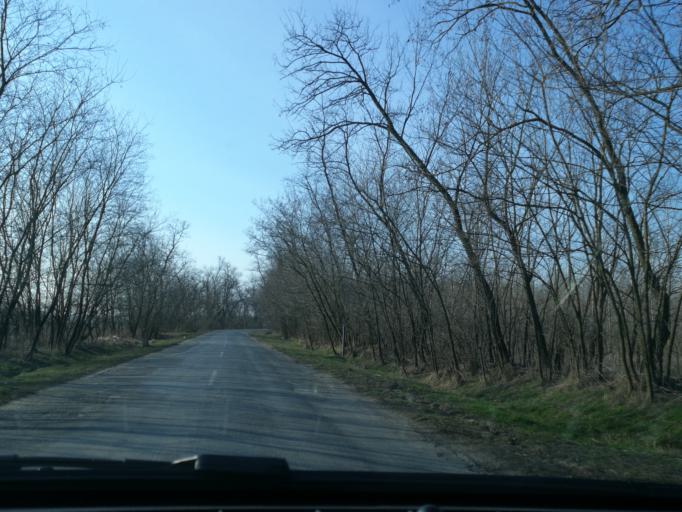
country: HU
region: Szabolcs-Szatmar-Bereg
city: Levelek
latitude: 48.0349
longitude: 21.9734
